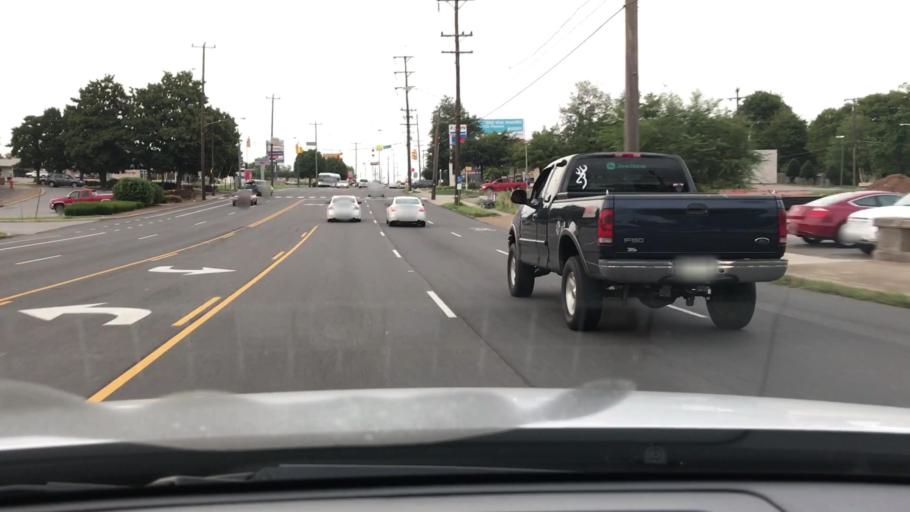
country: US
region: Tennessee
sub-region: Davidson County
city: Goodlettsville
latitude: 36.2524
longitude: -86.7173
